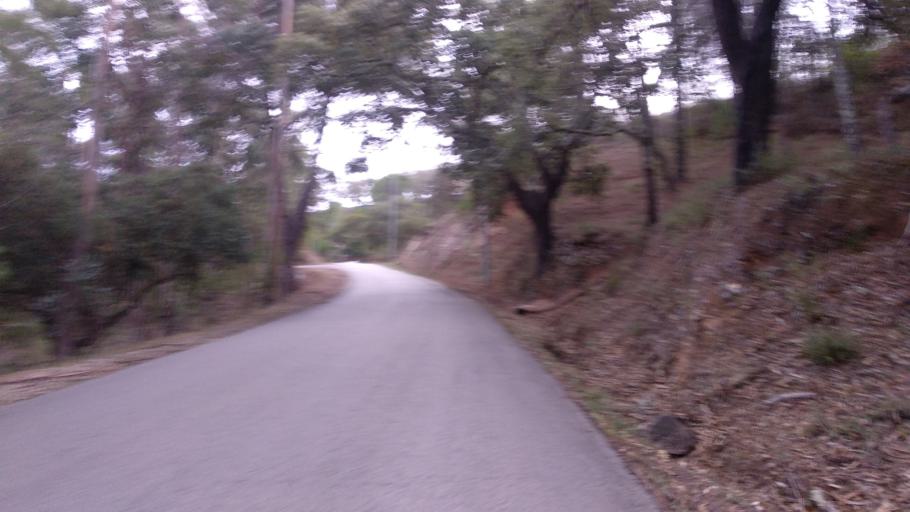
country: PT
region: Faro
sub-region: Sao Bras de Alportel
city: Sao Bras de Alportel
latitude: 37.1817
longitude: -7.9132
